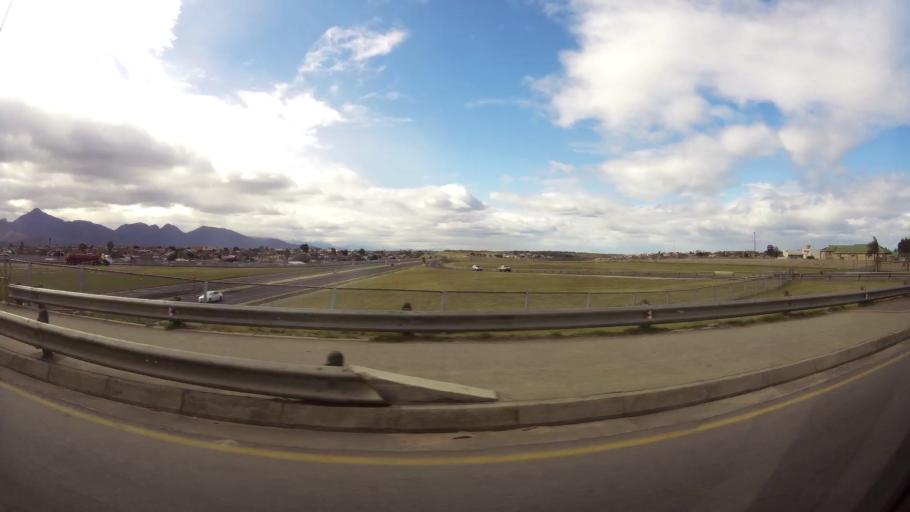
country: ZA
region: Western Cape
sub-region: Eden District Municipality
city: George
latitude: -33.9965
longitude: 22.4759
